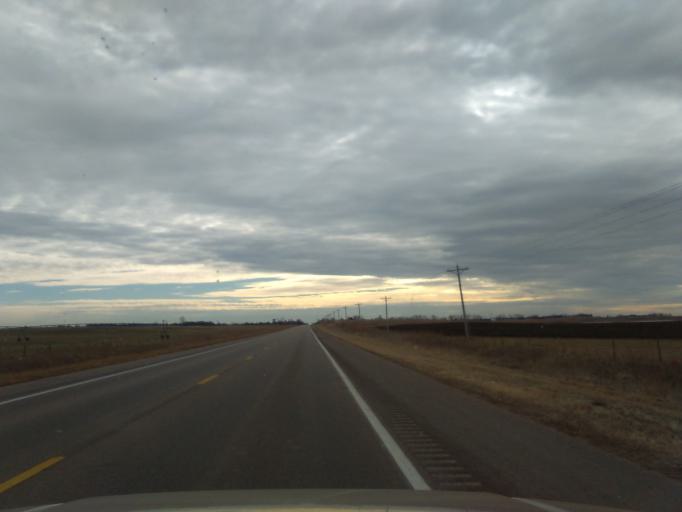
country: US
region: Nebraska
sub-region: Kearney County
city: Minden
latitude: 40.6249
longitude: -98.9515
